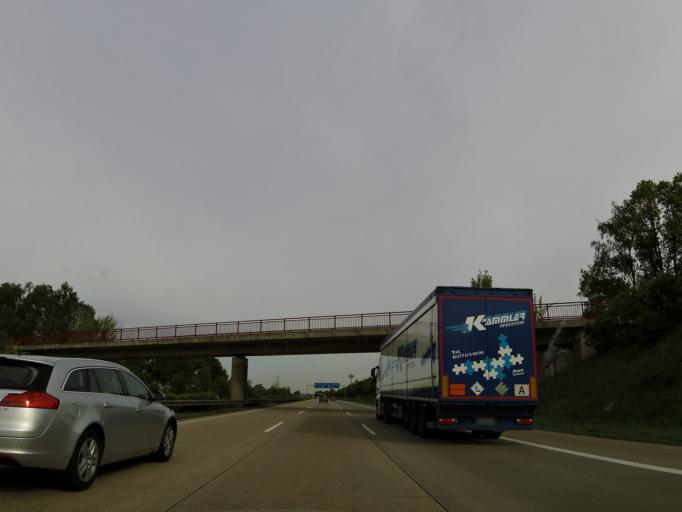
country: DE
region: Lower Saxony
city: Isernhagen Farster Bauerschaft
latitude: 52.4808
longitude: 9.8483
